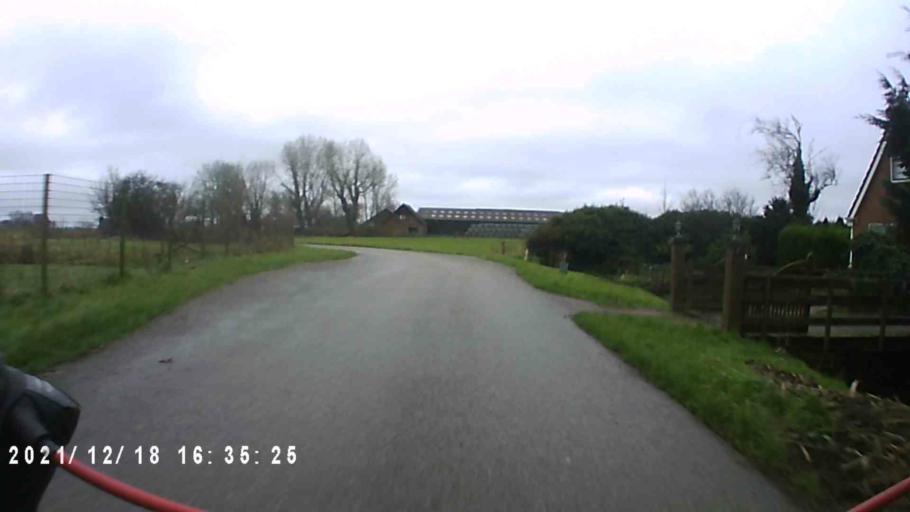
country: NL
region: Friesland
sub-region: Gemeente Dongeradeel
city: Dokkum
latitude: 53.3570
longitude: 6.0204
